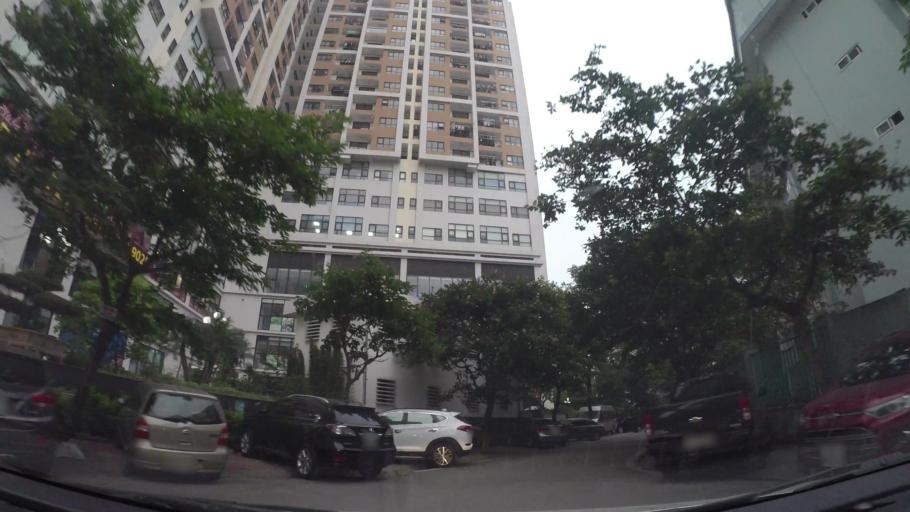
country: VN
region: Ha Noi
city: Cau Dien
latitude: 21.0357
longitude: 105.7657
